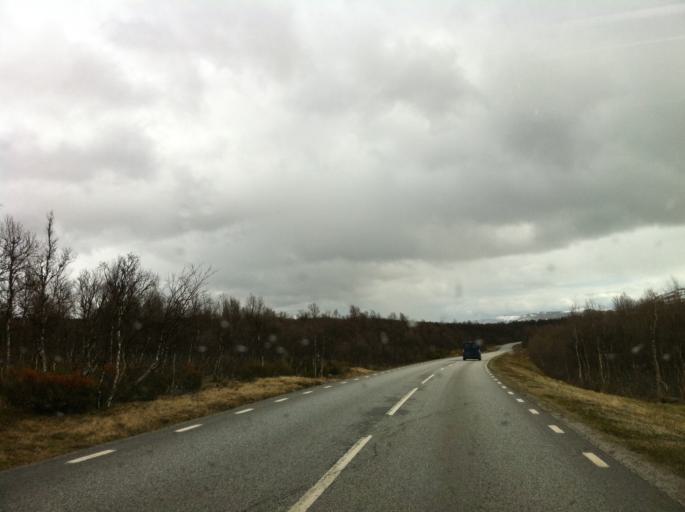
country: NO
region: Sor-Trondelag
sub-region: Tydal
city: Aas
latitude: 62.6368
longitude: 12.1070
